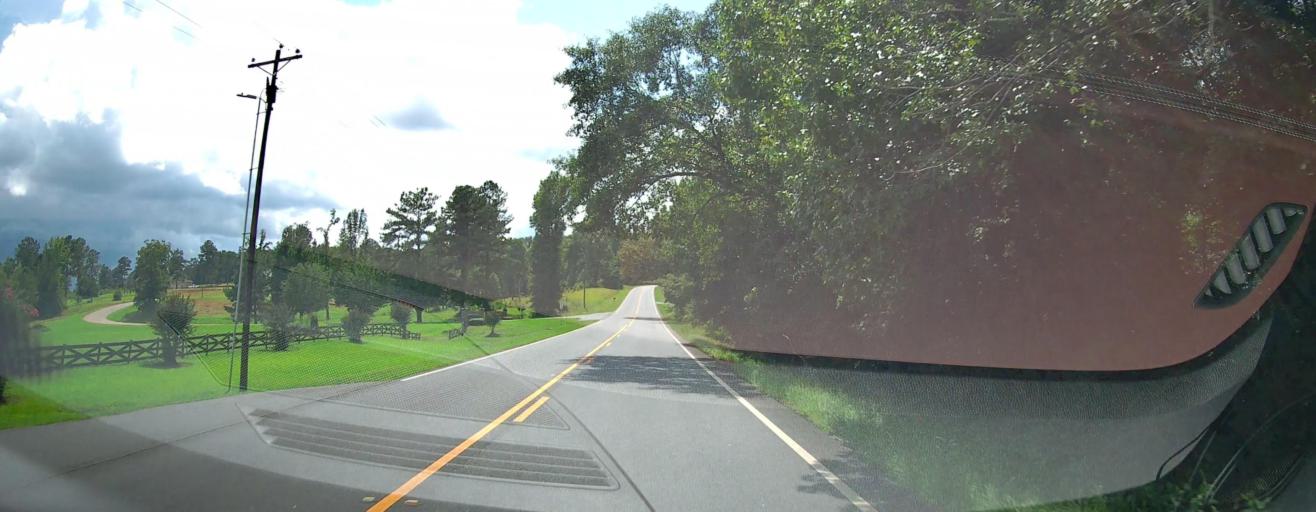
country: US
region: Georgia
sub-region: Crawford County
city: Knoxville
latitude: 32.8744
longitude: -83.9799
